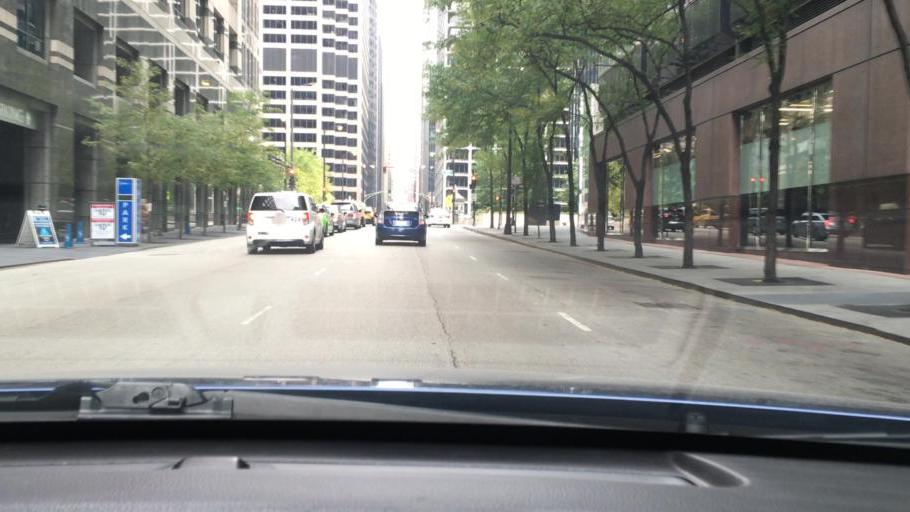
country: US
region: Illinois
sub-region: Cook County
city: Chicago
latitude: 41.8805
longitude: -87.6410
